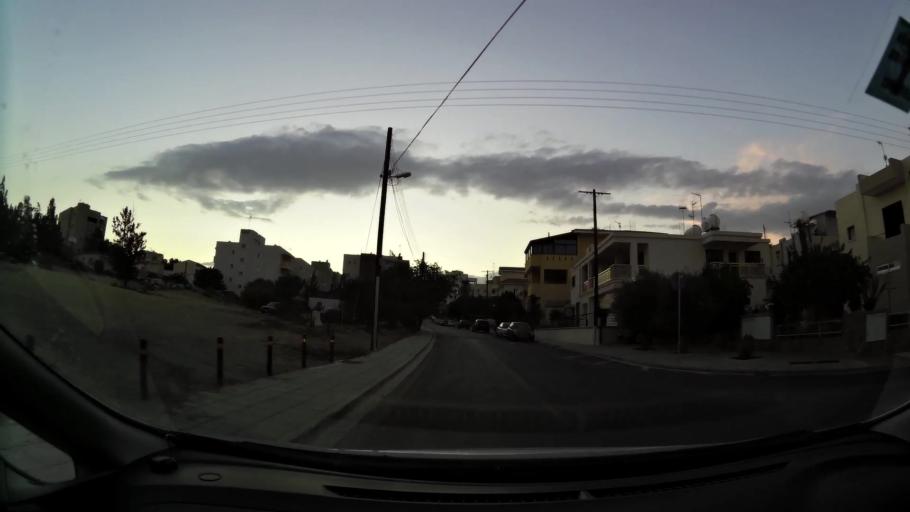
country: CY
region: Lefkosia
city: Nicosia
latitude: 35.1653
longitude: 33.3777
